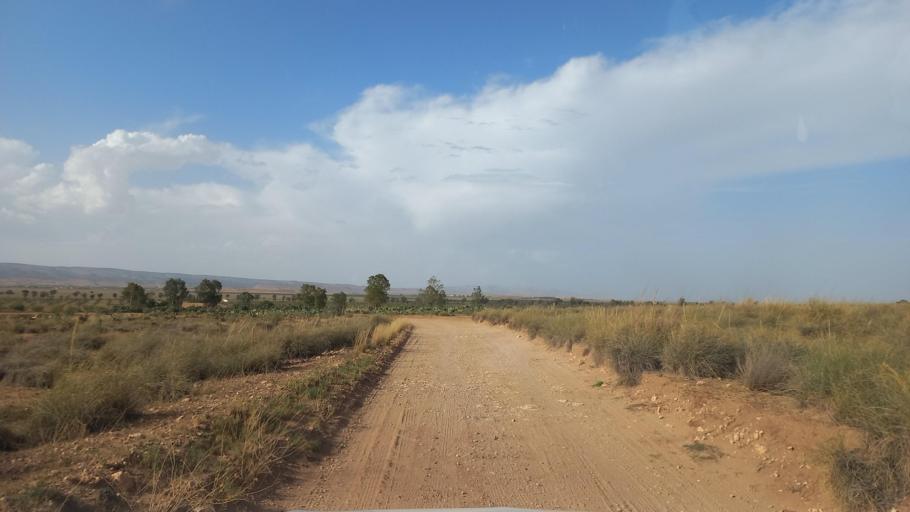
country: TN
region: Al Qasrayn
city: Kasserine
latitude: 35.2226
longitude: 8.9695
